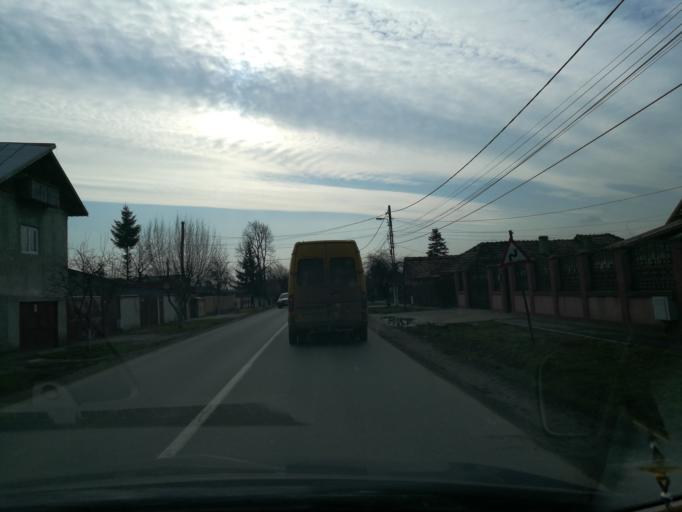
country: RO
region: Ilfov
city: Stefanestii de Jos
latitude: 44.5401
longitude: 26.2082
